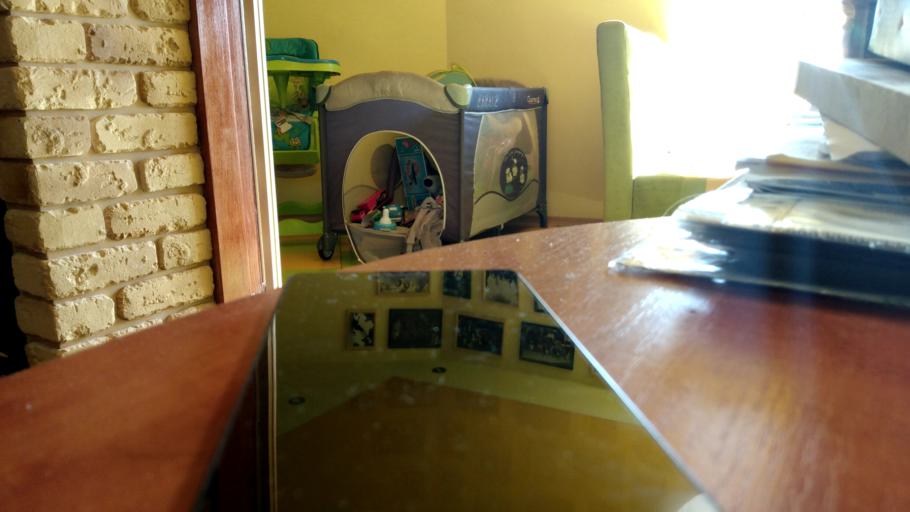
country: RU
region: Penza
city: Serdobsk
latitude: 52.3203
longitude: 44.3838
